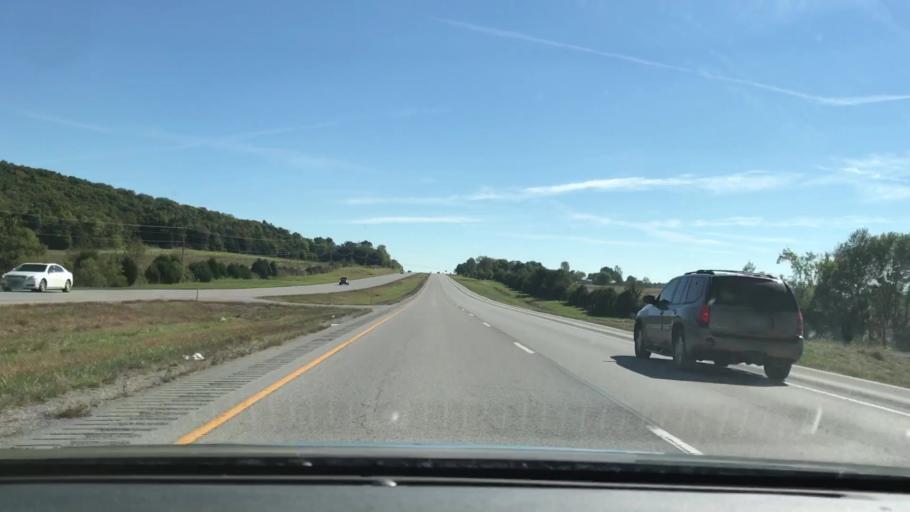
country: US
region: Kentucky
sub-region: Todd County
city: Elkton
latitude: 36.8252
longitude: -87.2125
